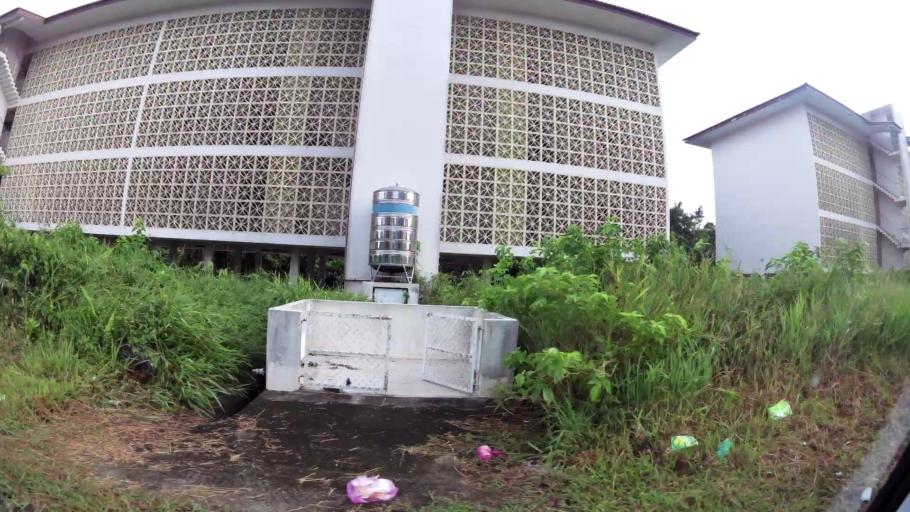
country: BN
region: Belait
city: Seria
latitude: 4.6159
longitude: 114.3345
